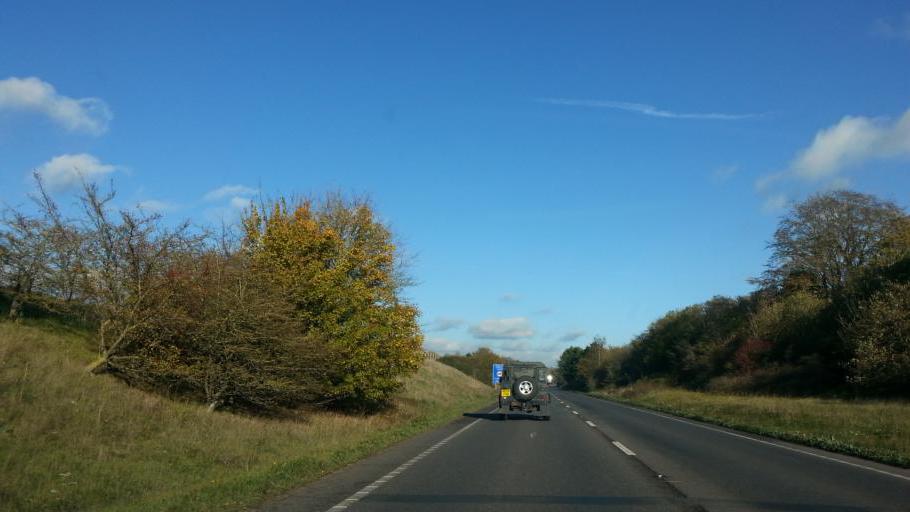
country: GB
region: England
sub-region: Norfolk
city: Harleston
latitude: 52.4188
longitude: 1.3478
